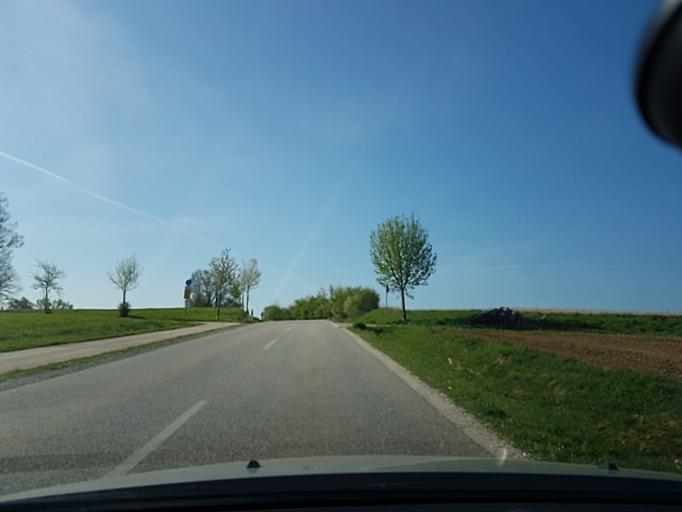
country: DE
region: Bavaria
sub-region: Lower Bavaria
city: Furth
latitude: 48.4127
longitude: 12.3718
